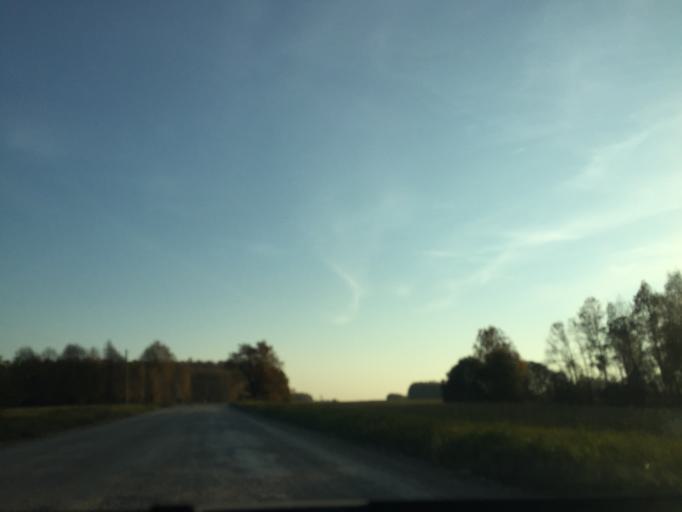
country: LV
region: Vainode
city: Vainode
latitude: 56.5409
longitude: 21.8366
